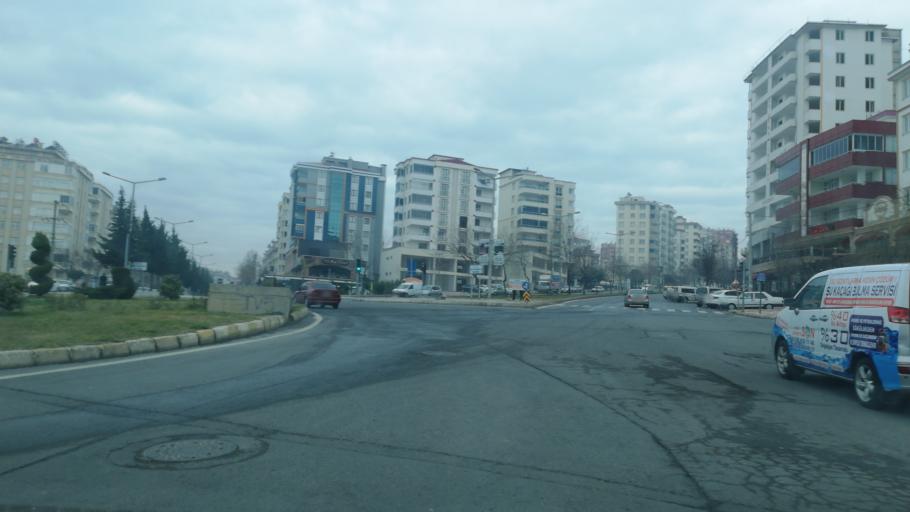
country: TR
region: Kahramanmaras
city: Kahramanmaras
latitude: 37.5928
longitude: 36.8992
